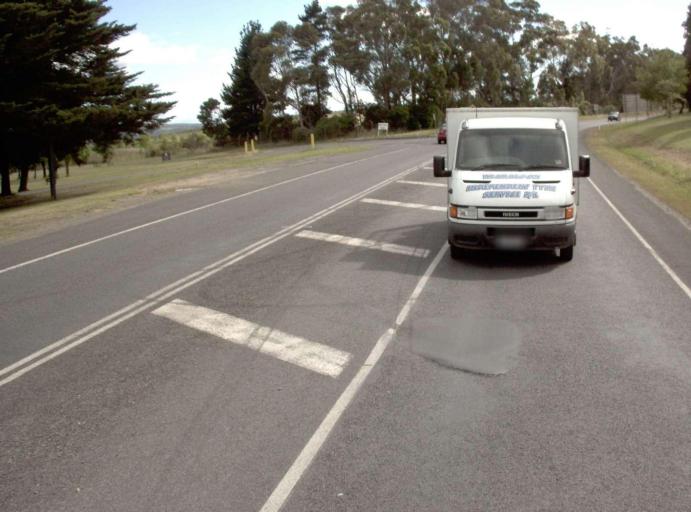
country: AU
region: Victoria
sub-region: Latrobe
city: Morwell
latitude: -38.1876
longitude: 146.4528
